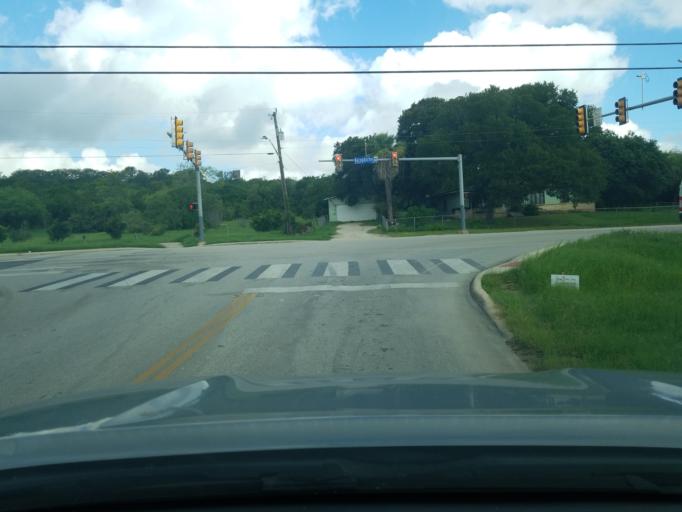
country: US
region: Texas
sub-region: Bexar County
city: Live Oak
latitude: 29.5831
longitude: -98.3653
